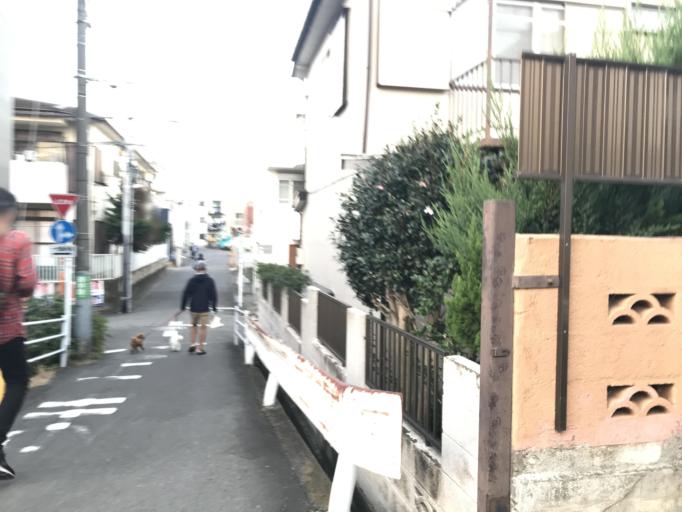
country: JP
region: Kanagawa
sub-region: Kawasaki-shi
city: Kawasaki
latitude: 35.5610
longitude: 139.6461
